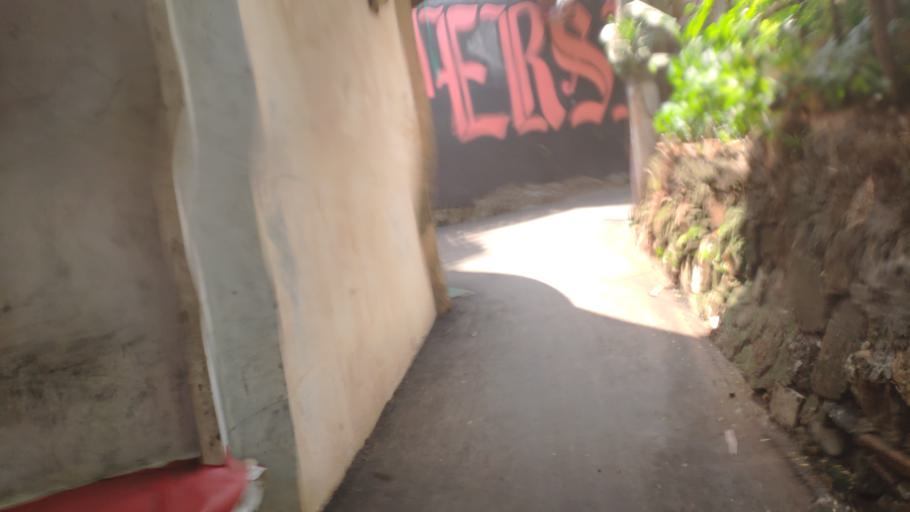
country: ID
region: Jakarta Raya
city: Jakarta
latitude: -6.2720
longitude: 106.8284
